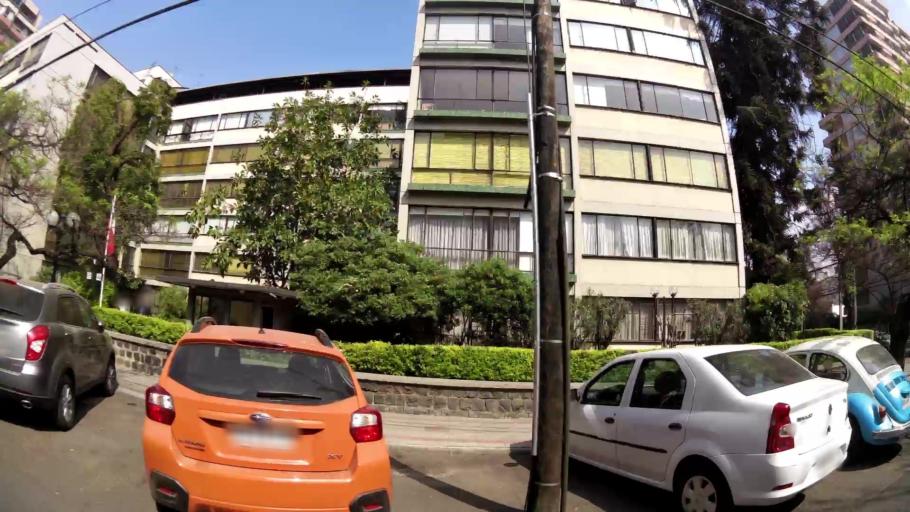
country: CL
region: Santiago Metropolitan
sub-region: Provincia de Santiago
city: Villa Presidente Frei, Nunoa, Santiago, Chile
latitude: -33.4224
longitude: -70.6002
